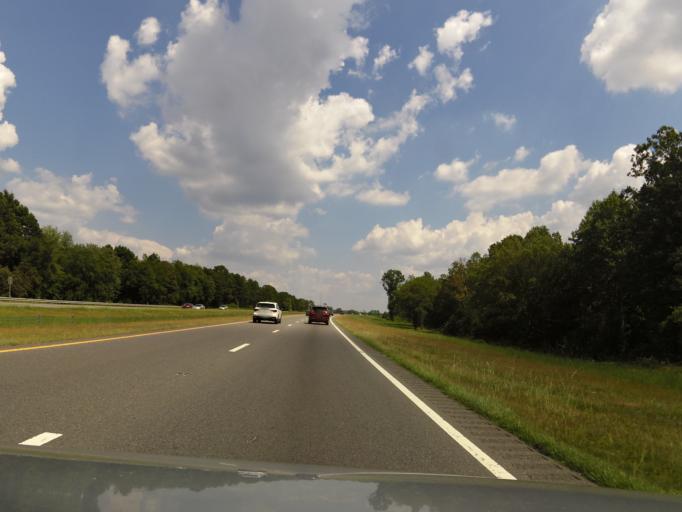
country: US
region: North Carolina
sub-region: Cleveland County
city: Kings Mountain
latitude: 35.2595
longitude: -81.3705
